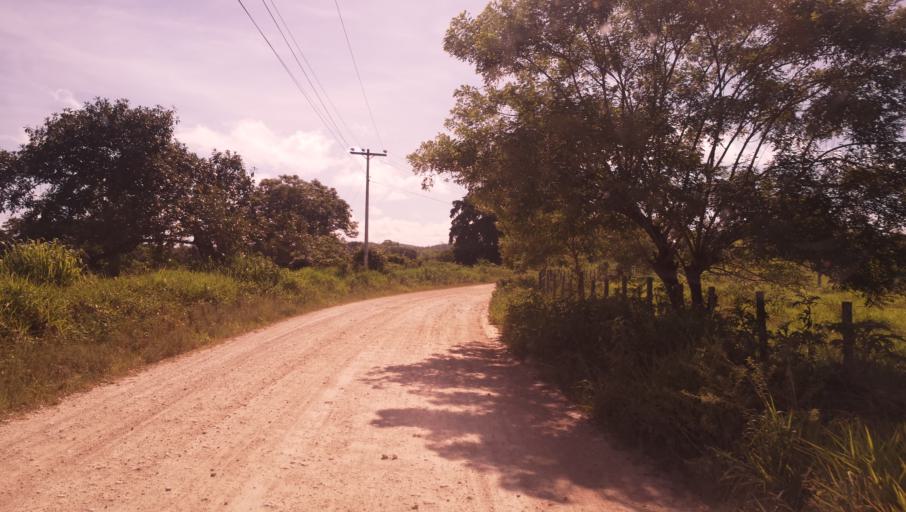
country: GT
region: Peten
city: Dolores
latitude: 16.7373
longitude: -89.3256
